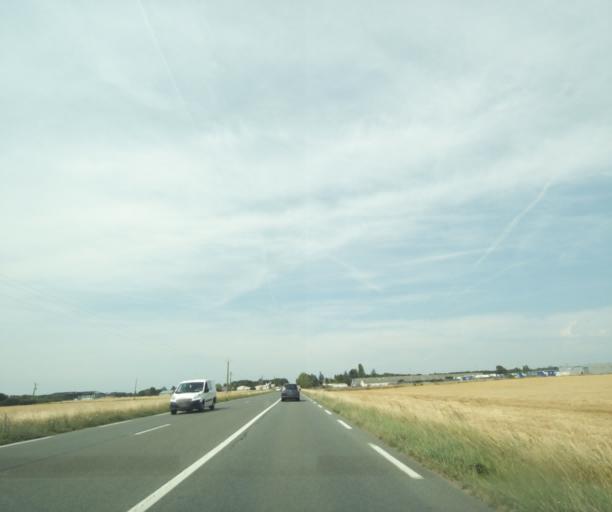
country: FR
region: Centre
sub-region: Departement d'Indre-et-Loire
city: Montbazon
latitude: 47.2639
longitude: 0.7041
